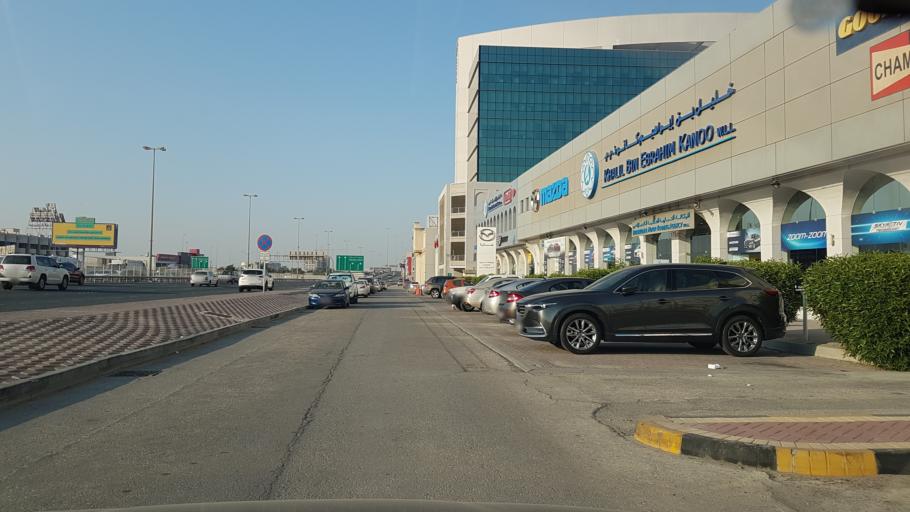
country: BH
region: Northern
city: Madinat `Isa
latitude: 26.1889
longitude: 50.5363
